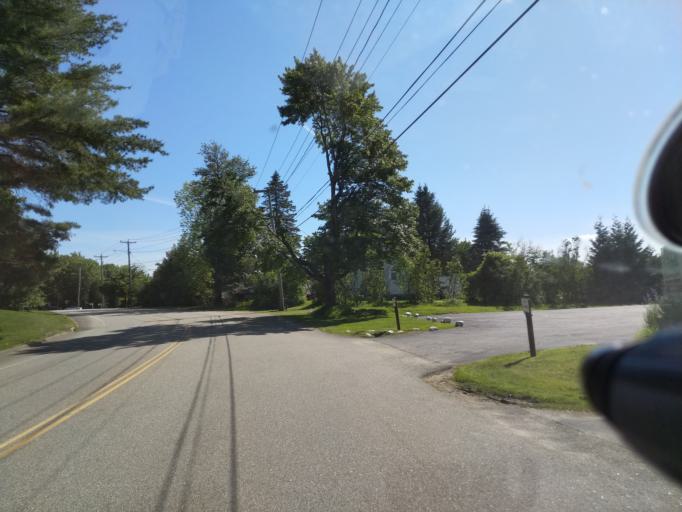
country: US
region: Maine
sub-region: Cumberland County
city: Falmouth
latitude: 43.7167
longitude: -70.3014
